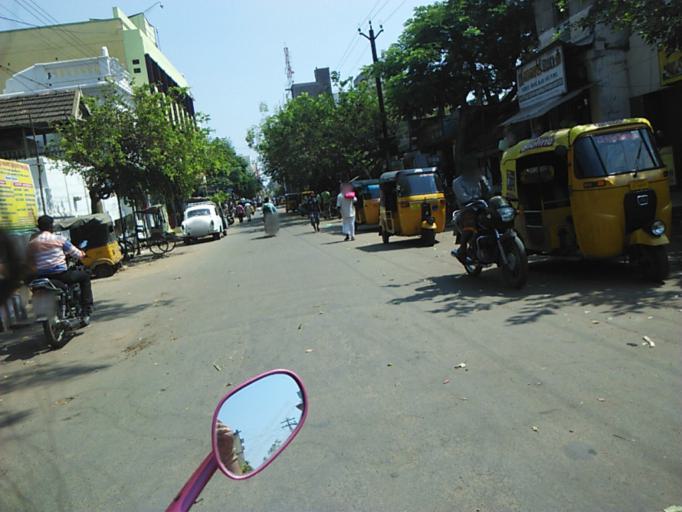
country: IN
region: Tamil Nadu
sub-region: Tiruchchirappalli
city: Tiruchirappalli
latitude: 10.8299
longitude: 78.6948
